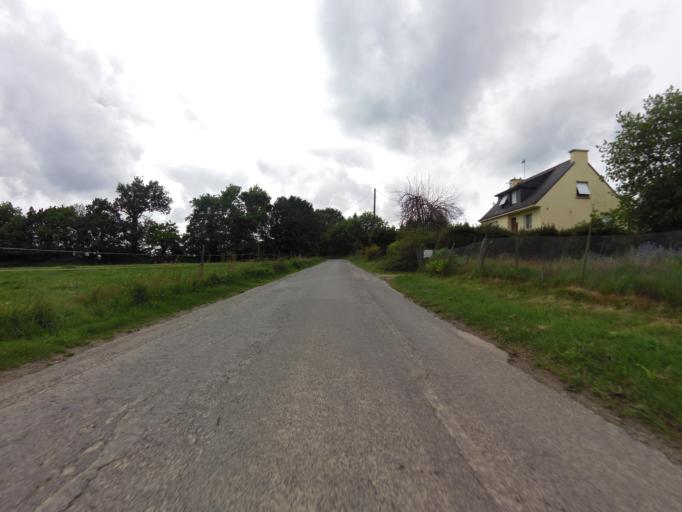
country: FR
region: Brittany
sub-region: Departement du Morbihan
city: Molac
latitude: 47.7299
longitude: -2.4520
